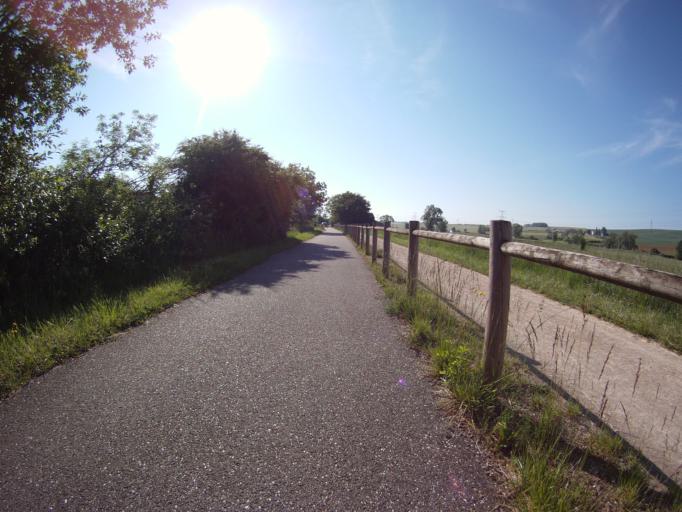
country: FR
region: Lorraine
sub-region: Departement de Meurthe-et-Moselle
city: Seichamps
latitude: 48.7387
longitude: 6.2535
